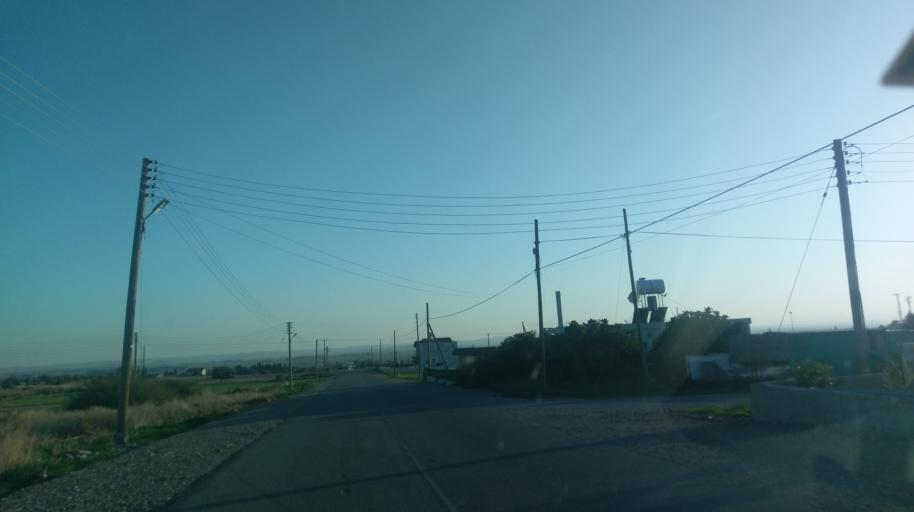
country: CY
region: Ammochostos
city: Lefkonoiko
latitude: 35.2401
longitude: 33.5546
